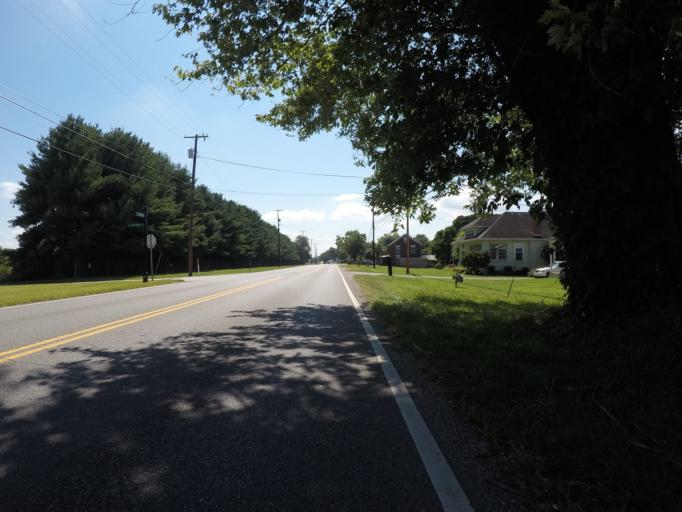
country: US
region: Ohio
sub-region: Lawrence County
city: South Point
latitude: 38.4302
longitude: -82.5937
